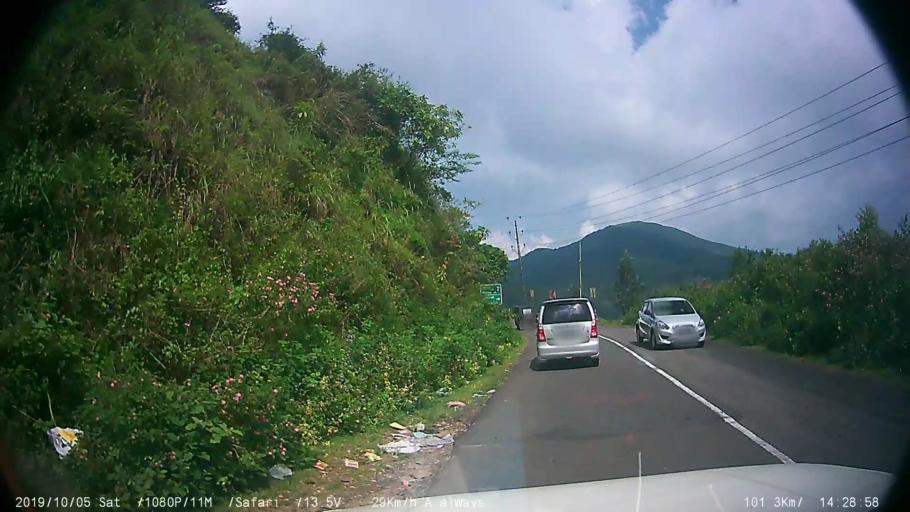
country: IN
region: Kerala
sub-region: Kottayam
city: Erattupetta
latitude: 9.6085
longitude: 76.9659
